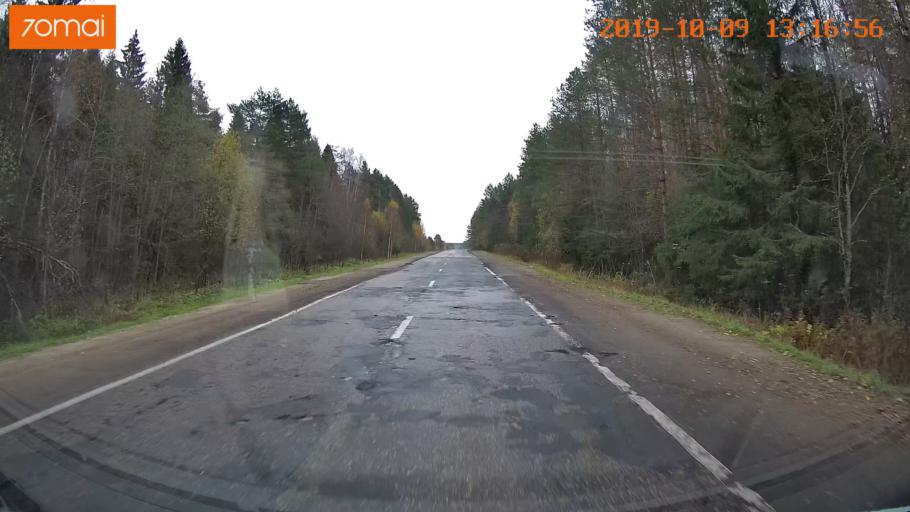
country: RU
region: Jaroslavl
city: Lyubim
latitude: 58.3576
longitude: 40.7728
